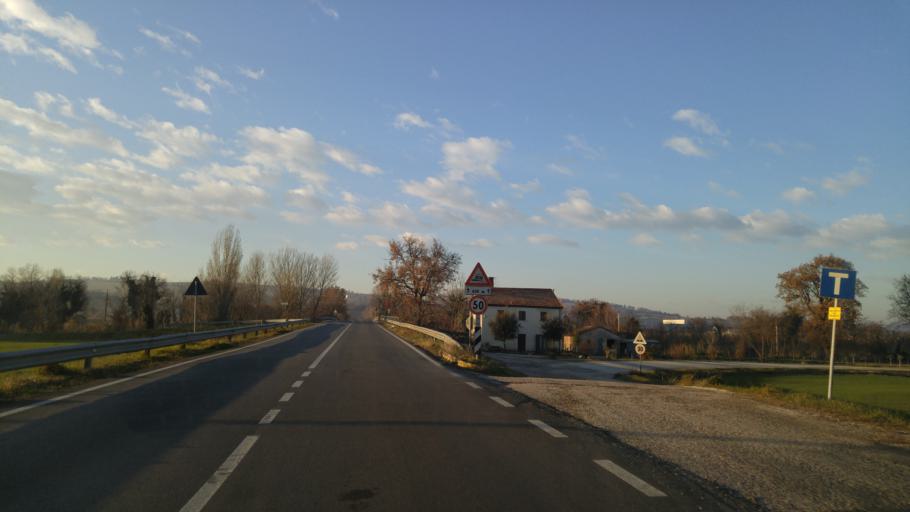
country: IT
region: The Marches
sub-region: Provincia di Ancona
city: Monterado
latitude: 43.7051
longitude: 13.0827
